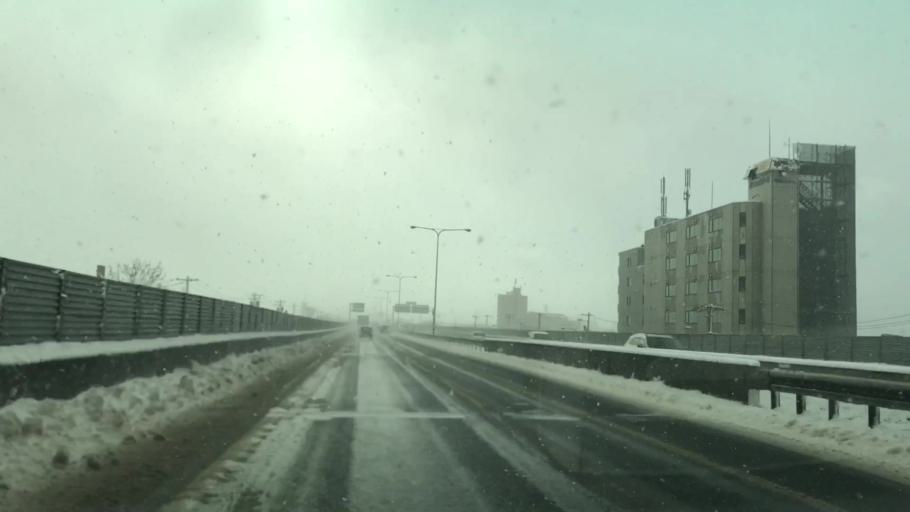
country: JP
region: Hokkaido
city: Sapporo
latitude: 43.0678
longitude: 141.4229
